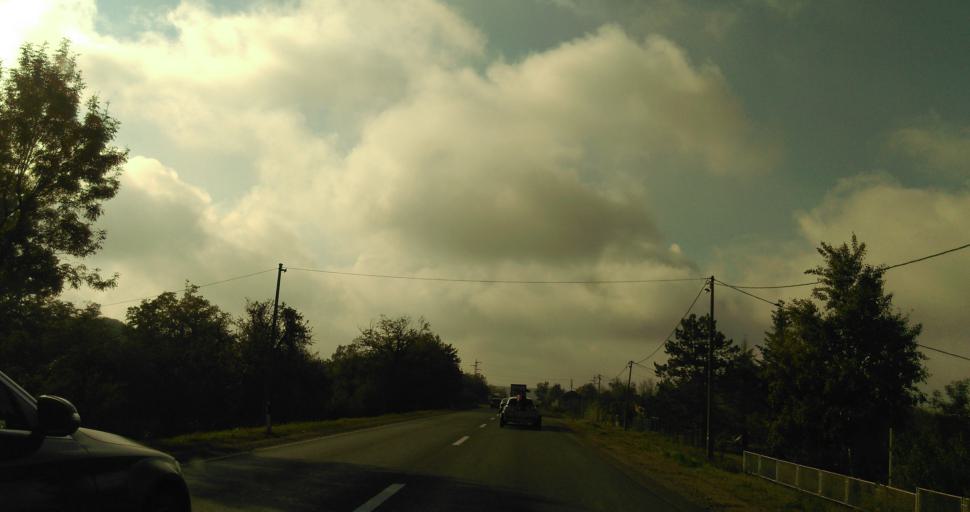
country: RS
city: Stepojevac
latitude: 44.5492
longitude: 20.3003
